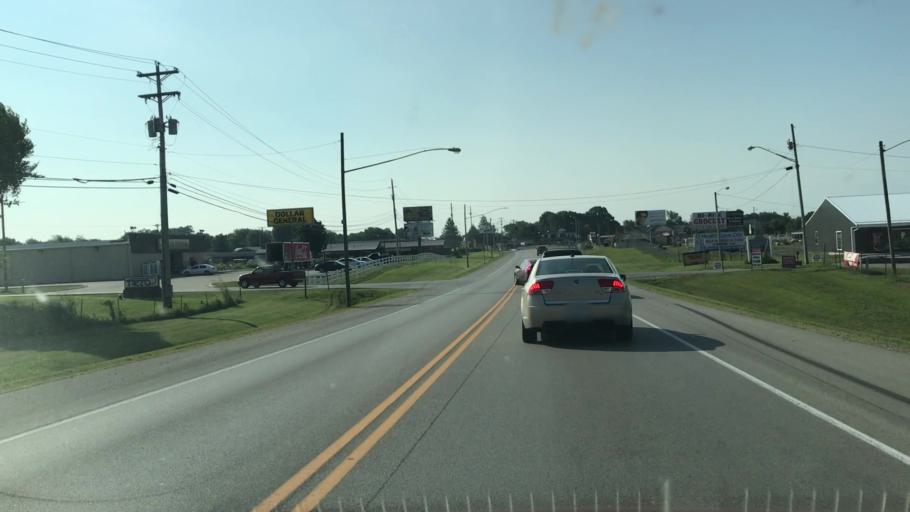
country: US
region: Kentucky
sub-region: Barren County
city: Cave City
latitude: 37.1299
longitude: -85.9654
